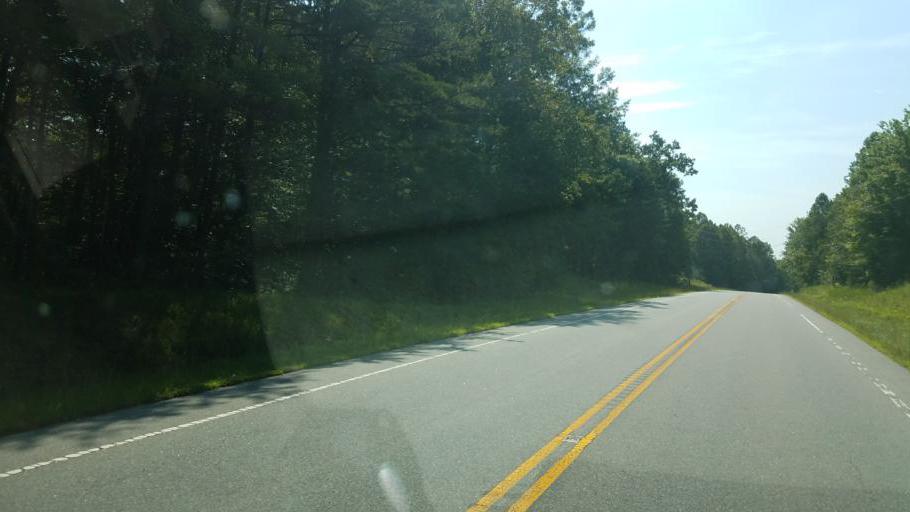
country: US
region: North Carolina
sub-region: Burke County
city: Glen Alpine
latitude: 35.8879
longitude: -81.8022
